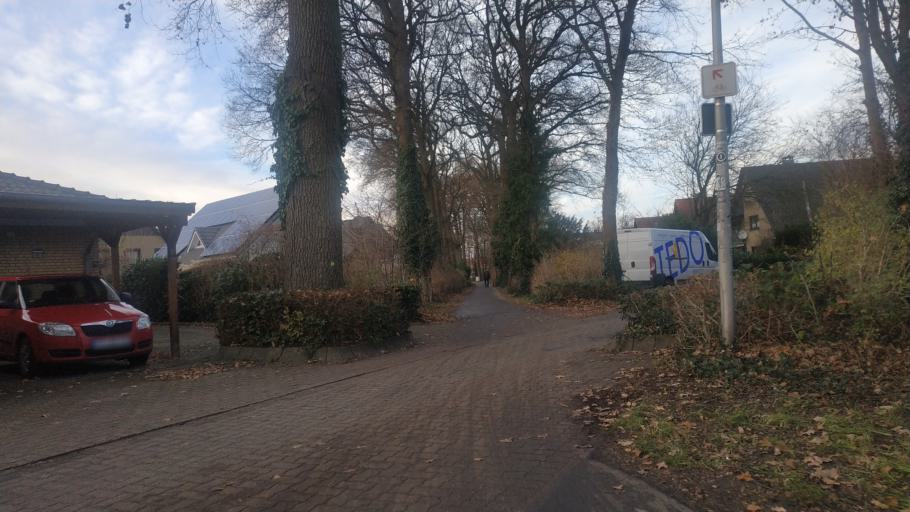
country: DE
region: North Rhine-Westphalia
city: Ibbenburen
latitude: 52.2735
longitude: 7.6974
